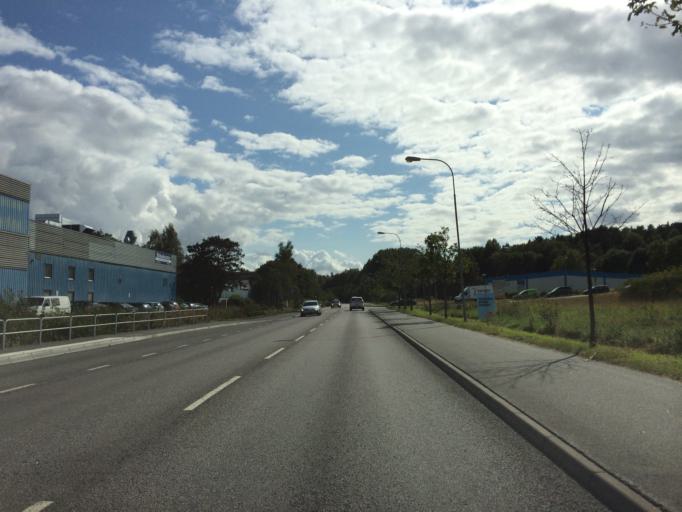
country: SE
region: Stockholm
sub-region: Sollentuna Kommun
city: Sollentuna
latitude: 59.4348
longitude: 17.9310
